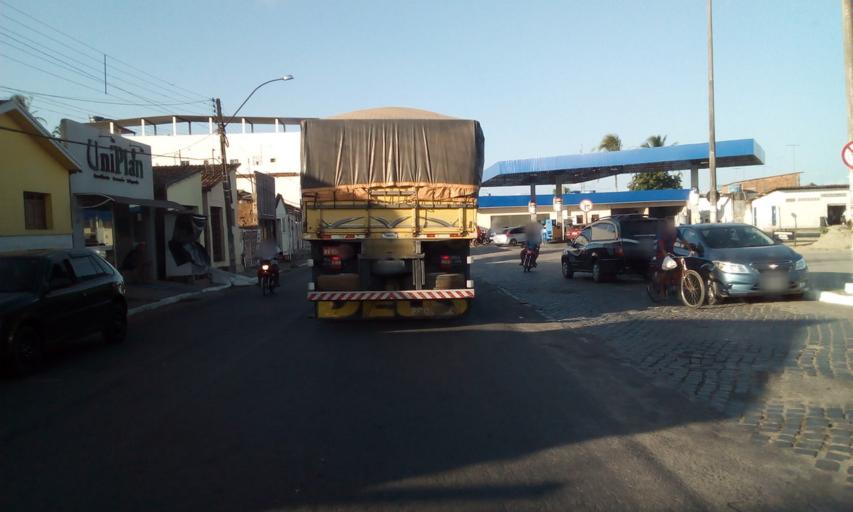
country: BR
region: Paraiba
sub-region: Mari
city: Mari
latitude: -7.0931
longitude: -35.2338
